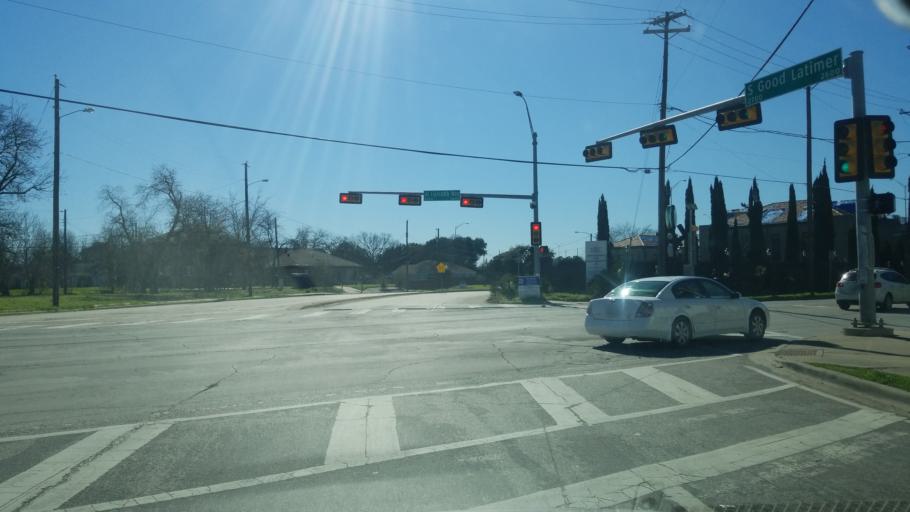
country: US
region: Texas
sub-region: Dallas County
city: Dallas
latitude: 32.7684
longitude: -96.7757
